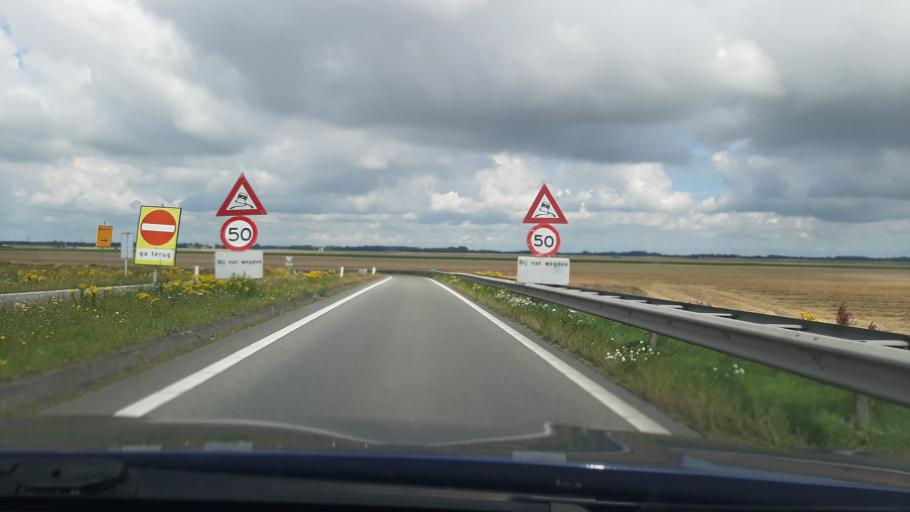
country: NL
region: Groningen
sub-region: Gemeente  Oldambt
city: Winschoten
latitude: 53.1866
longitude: 6.9758
